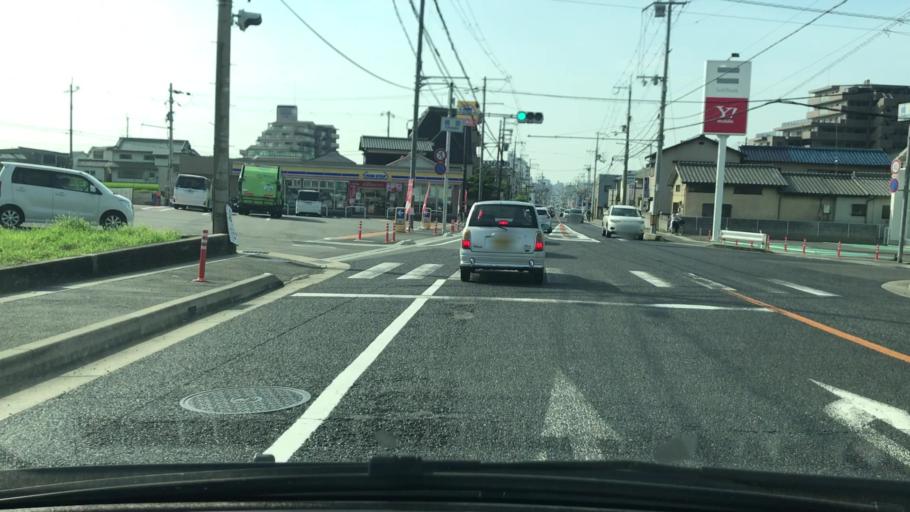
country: JP
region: Hyogo
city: Kakogawacho-honmachi
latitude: 34.7164
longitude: 134.8979
